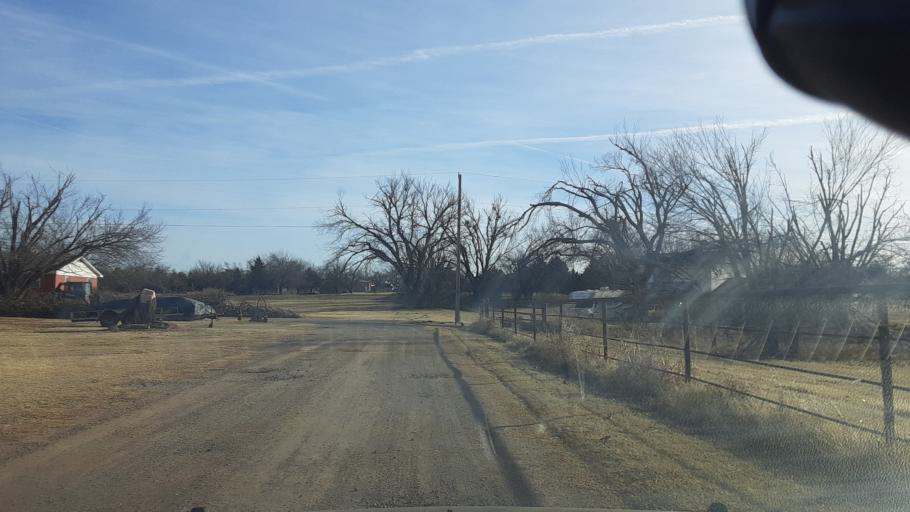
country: US
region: Oklahoma
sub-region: Logan County
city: Guthrie
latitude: 35.8527
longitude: -97.4315
